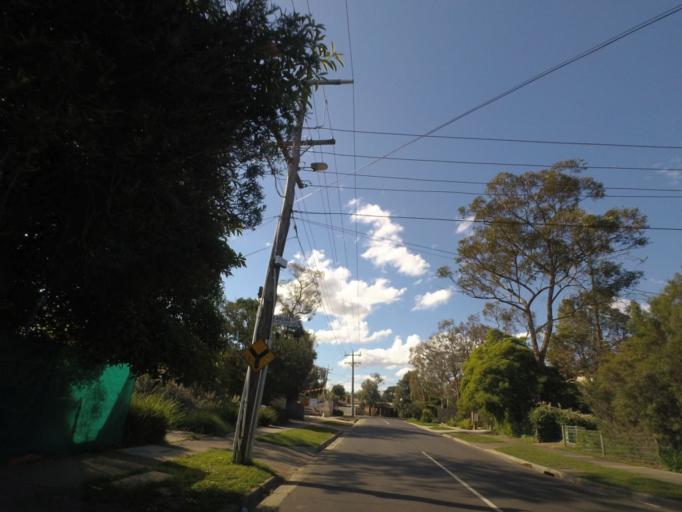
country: AU
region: Victoria
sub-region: Knox
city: Knoxfield
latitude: -37.8868
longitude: 145.2491
